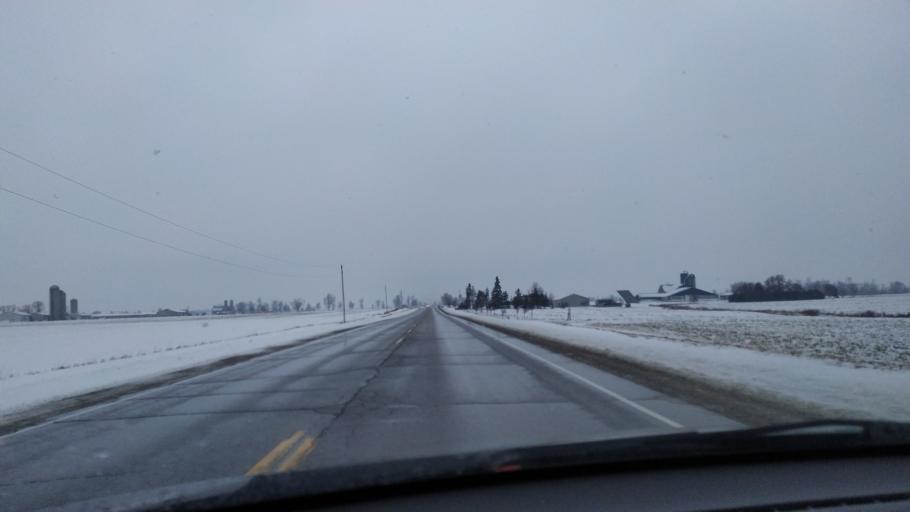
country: CA
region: Ontario
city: Stratford
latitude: 43.5382
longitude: -80.8655
